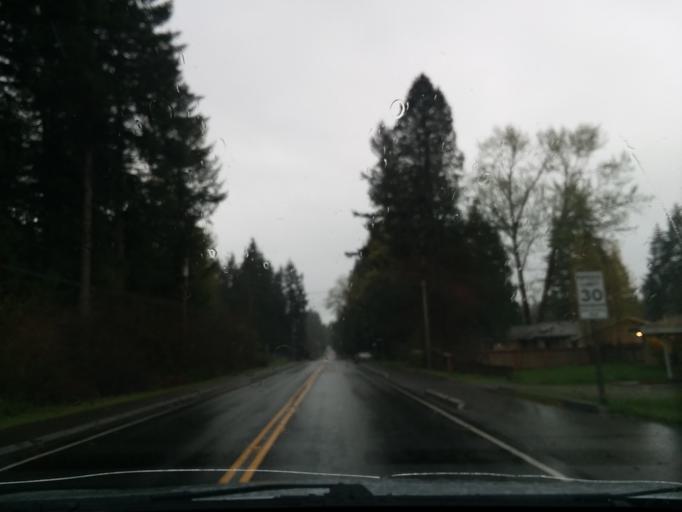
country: US
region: Washington
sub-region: King County
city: Fairwood
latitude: 47.4802
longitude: -122.1483
